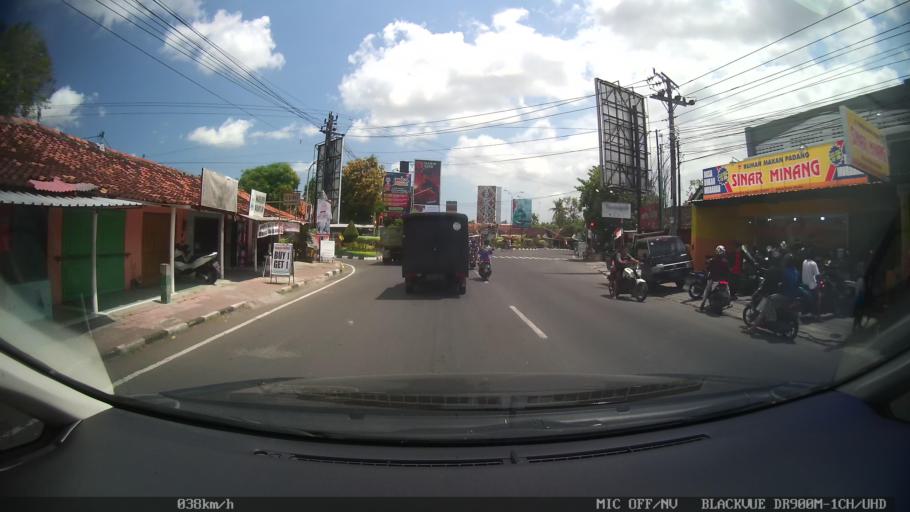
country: ID
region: Daerah Istimewa Yogyakarta
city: Bantul
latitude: -7.8928
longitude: 110.3353
